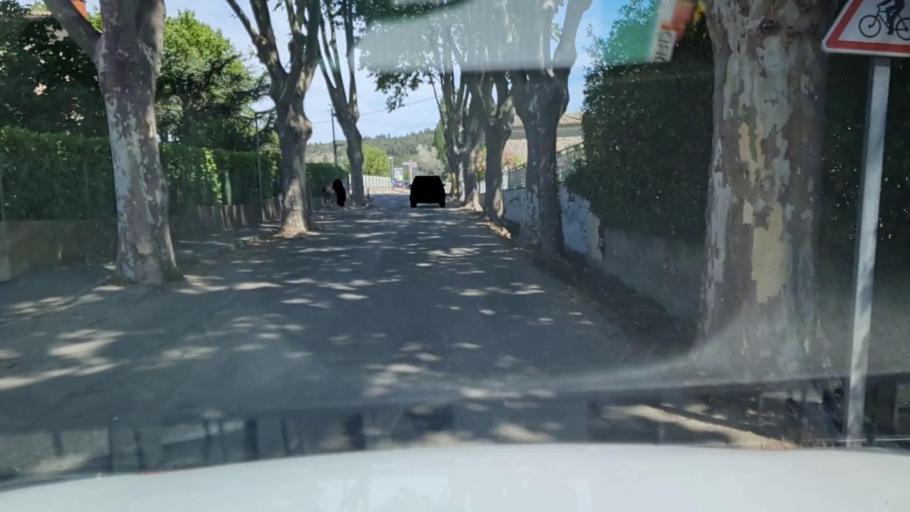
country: FR
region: Languedoc-Roussillon
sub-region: Departement du Gard
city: Clarensac
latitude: 43.8271
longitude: 4.2245
